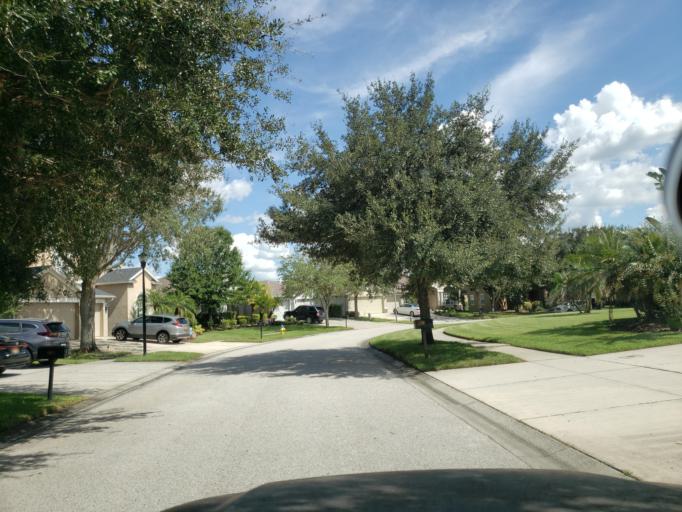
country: US
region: Florida
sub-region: Hillsborough County
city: Fish Hawk
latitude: 27.8378
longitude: -82.2141
